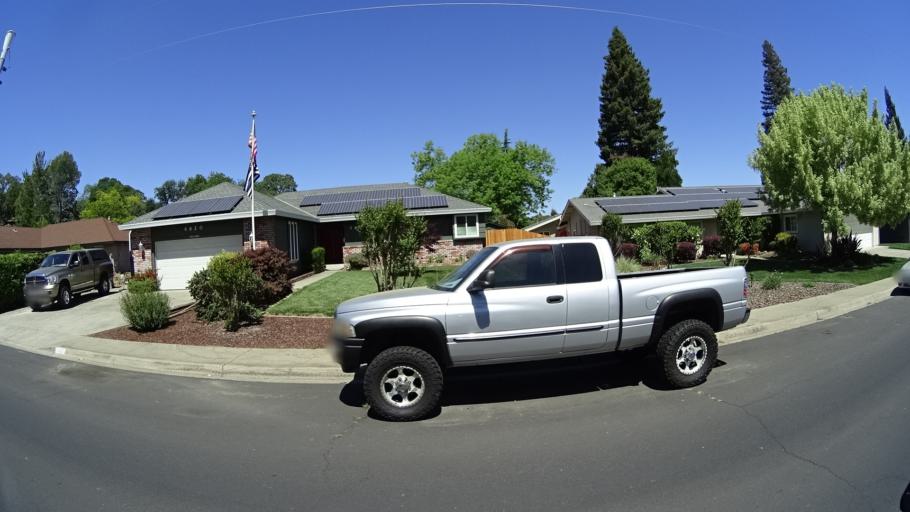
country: US
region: California
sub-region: Placer County
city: Rocklin
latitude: 38.7970
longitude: -121.2530
